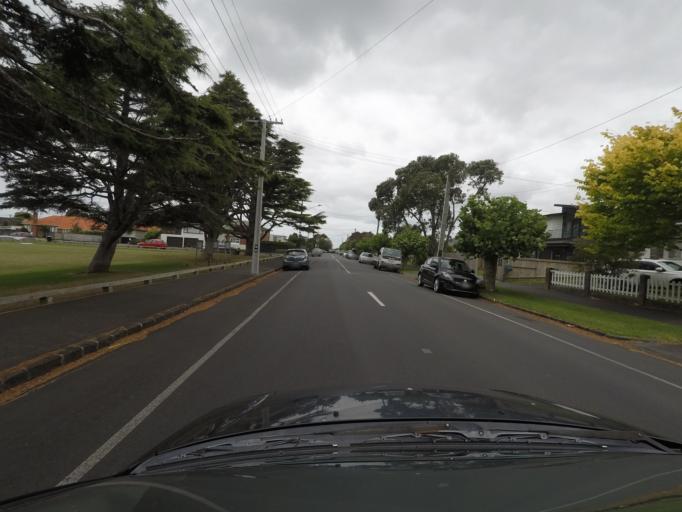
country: NZ
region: Auckland
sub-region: Auckland
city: Rosebank
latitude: -36.8656
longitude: 174.7044
